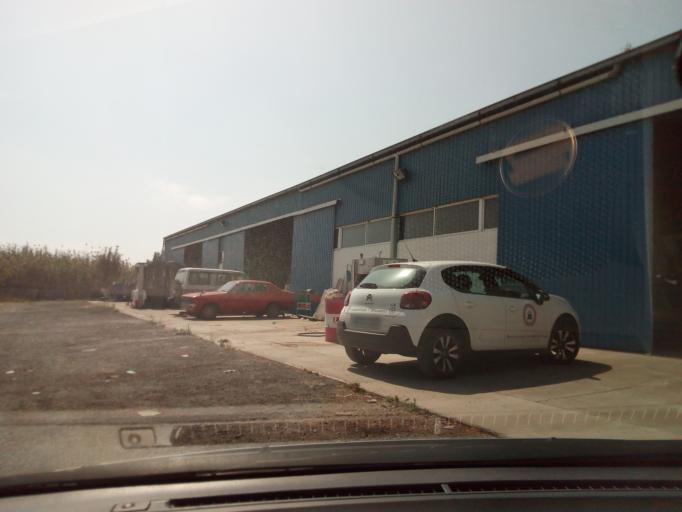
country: CY
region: Larnaka
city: Livadia
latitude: 34.9429
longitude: 33.6333
